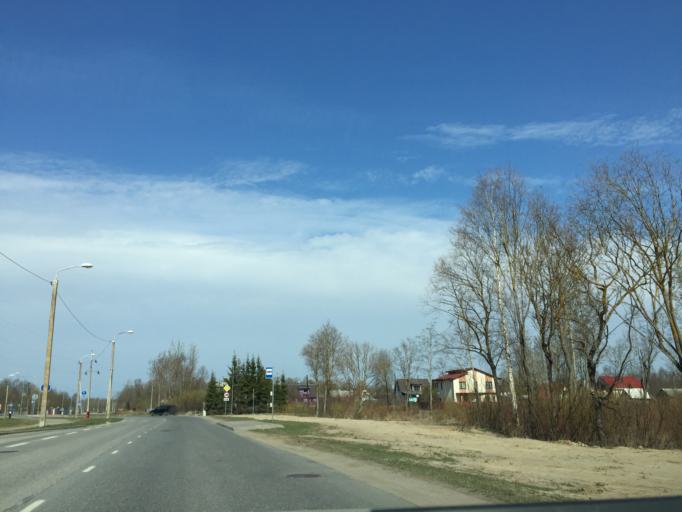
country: EE
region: Ida-Virumaa
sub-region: Narva linn
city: Narva
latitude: 59.3928
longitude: 28.1833
